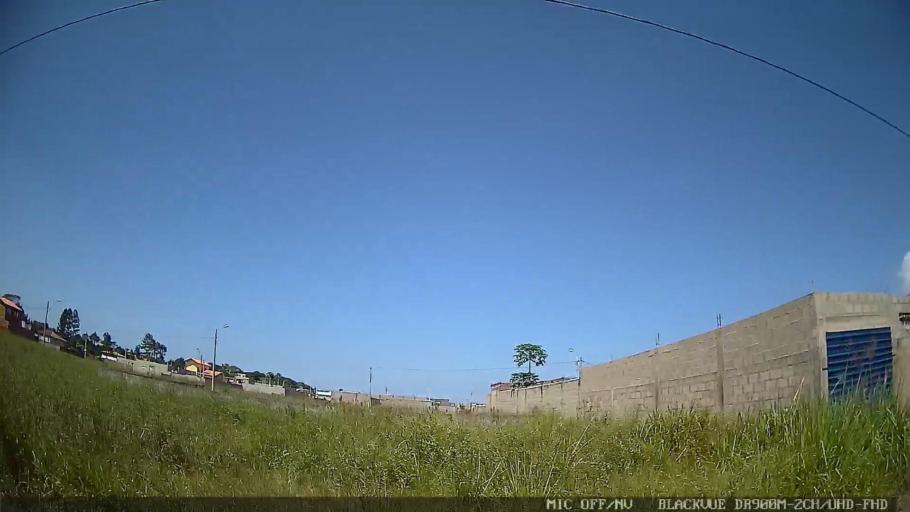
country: BR
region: Sao Paulo
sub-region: Peruibe
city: Peruibe
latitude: -24.2959
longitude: -47.0032
